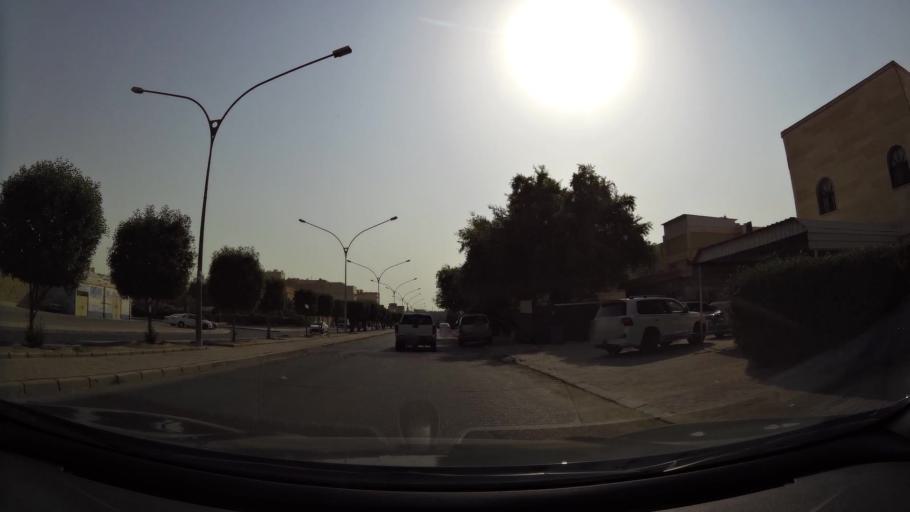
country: KW
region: Muhafazat al Jahra'
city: Al Jahra'
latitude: 29.3392
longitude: 47.7015
